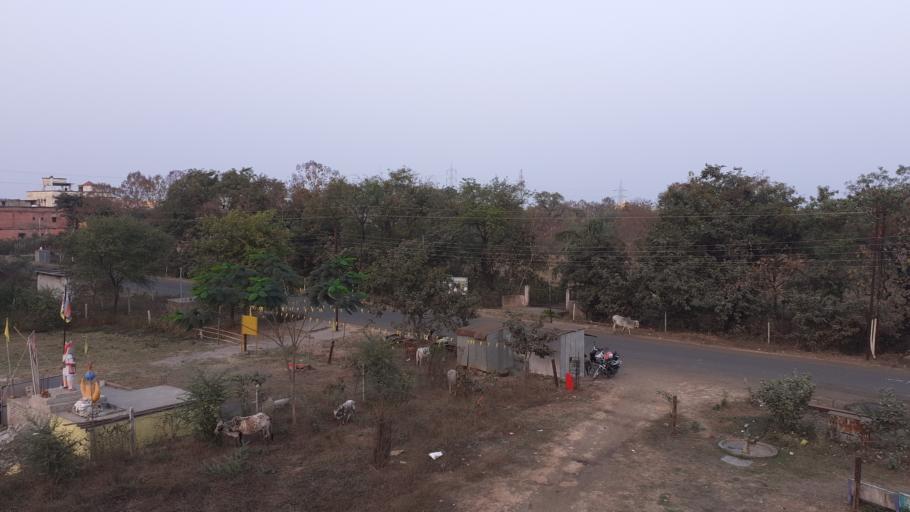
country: IN
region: Maharashtra
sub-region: Chandrapur
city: Warora
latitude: 20.2347
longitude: 79.0128
